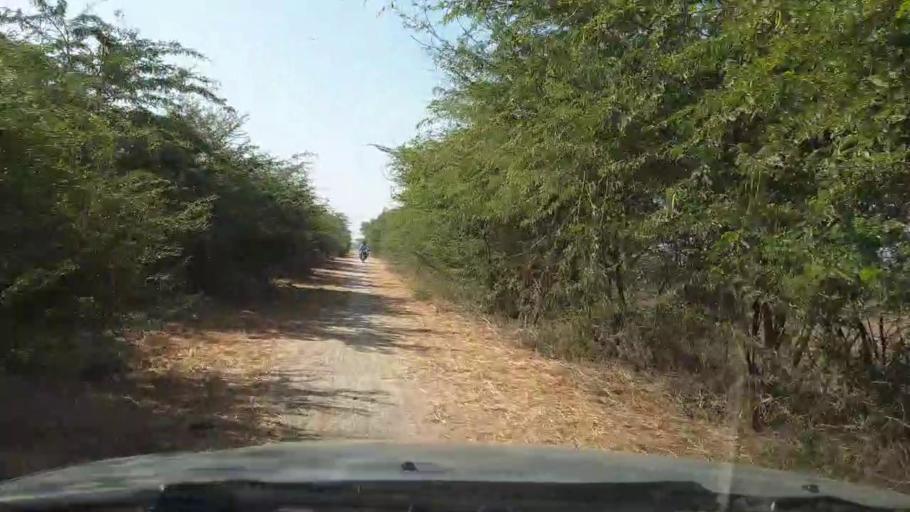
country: PK
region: Sindh
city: Kario
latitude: 24.8991
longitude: 68.5663
